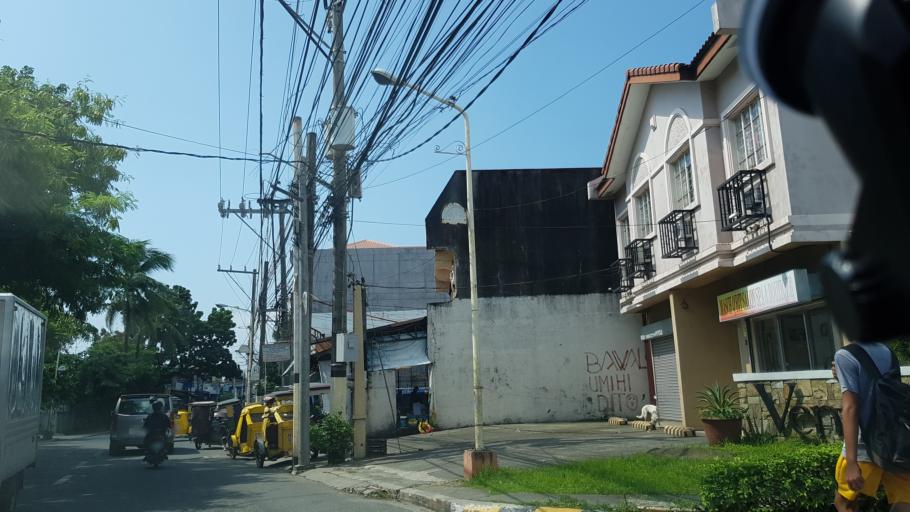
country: PH
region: Calabarzon
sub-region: Province of Rizal
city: Las Pinas
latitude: 14.4690
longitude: 120.9800
